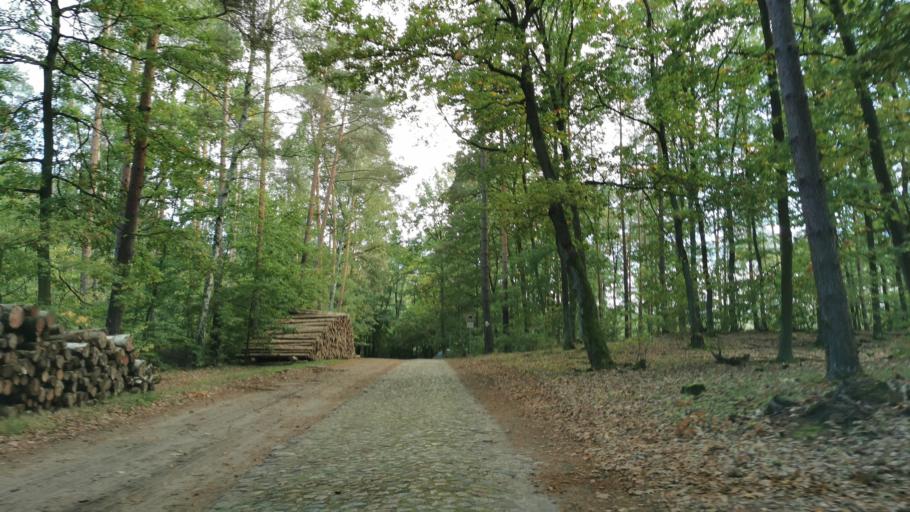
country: DE
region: Brandenburg
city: Michendorf
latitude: 52.3135
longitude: 12.9726
